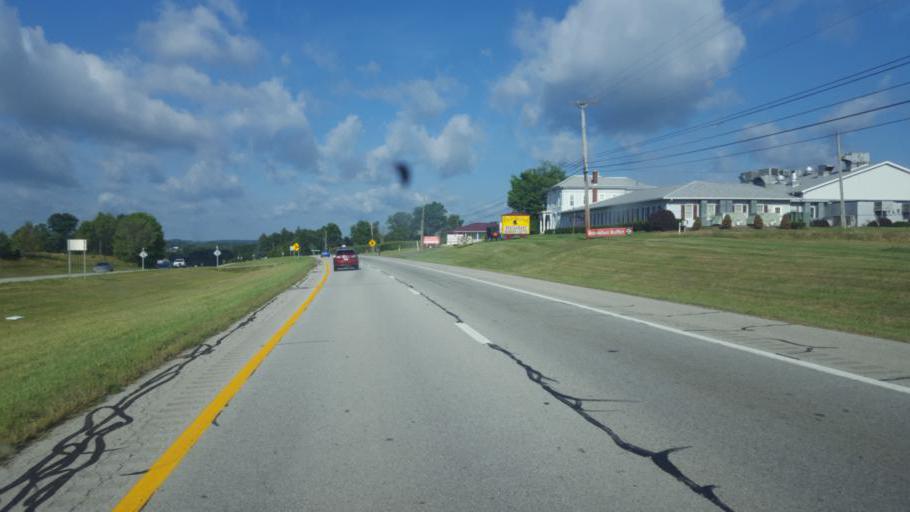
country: US
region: Ohio
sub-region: Wayne County
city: Dalton
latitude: 40.8010
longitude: -81.7268
